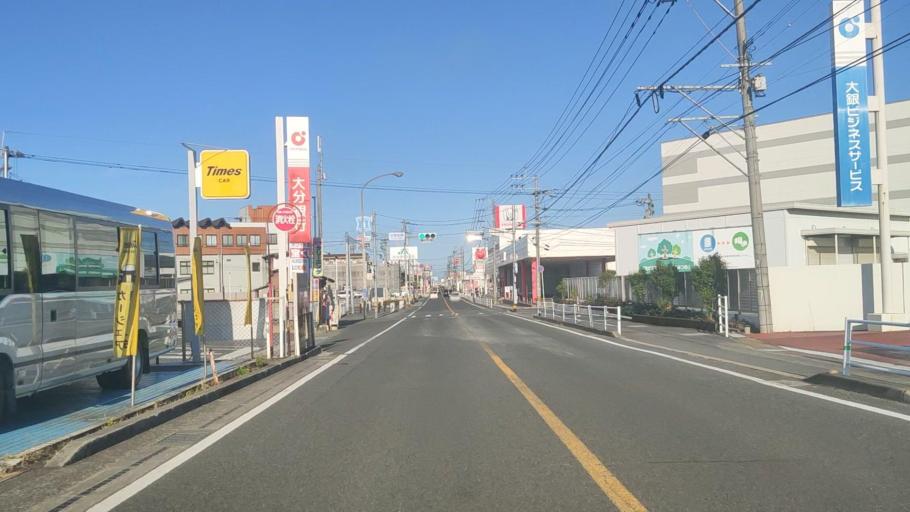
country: JP
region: Oita
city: Oita
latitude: 33.2118
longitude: 131.6083
